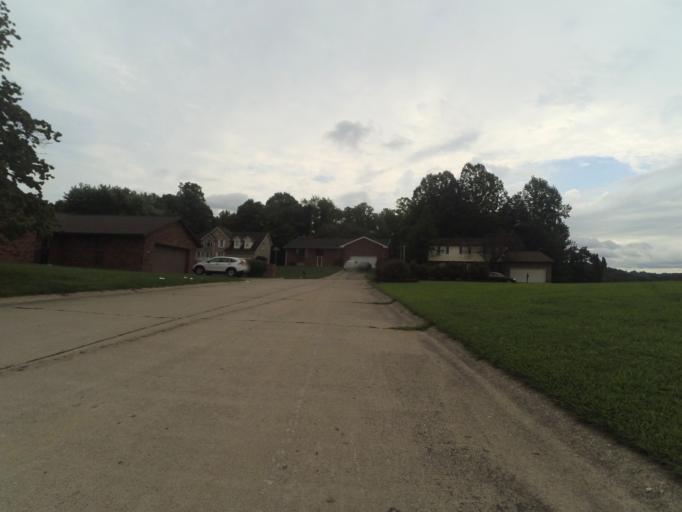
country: US
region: West Virginia
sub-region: Cabell County
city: Huntington
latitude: 38.4006
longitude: -82.3922
